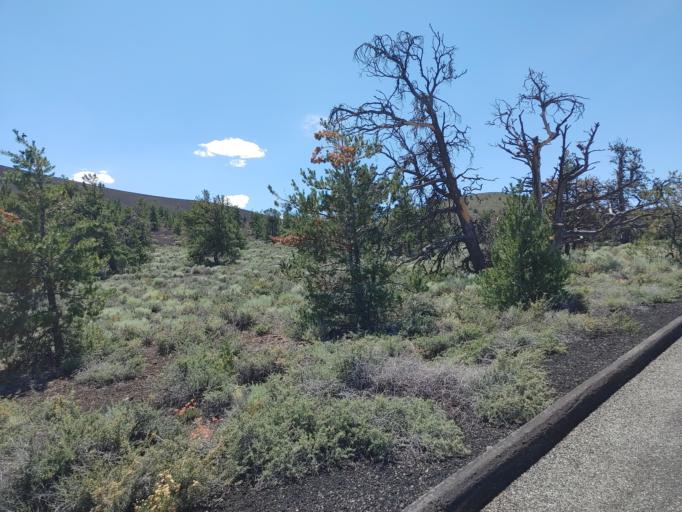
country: US
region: Idaho
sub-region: Butte County
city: Arco
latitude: 43.4469
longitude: -113.5513
